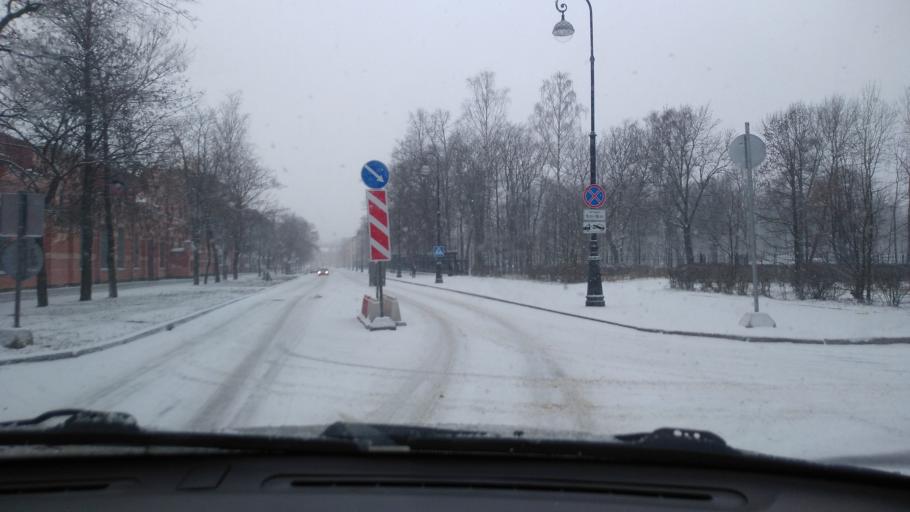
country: RU
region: St.-Petersburg
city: Kronshtadt
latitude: 59.9867
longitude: 29.7800
